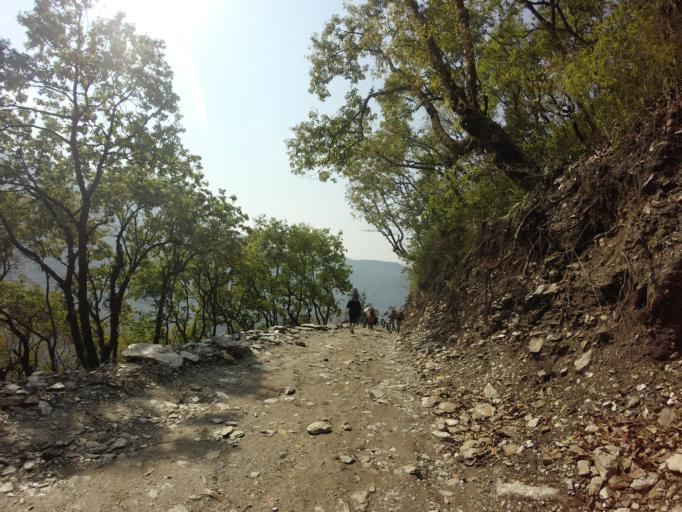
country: NP
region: Western Region
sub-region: Dhawalagiri Zone
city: Chitre
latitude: 28.3671
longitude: 83.8102
